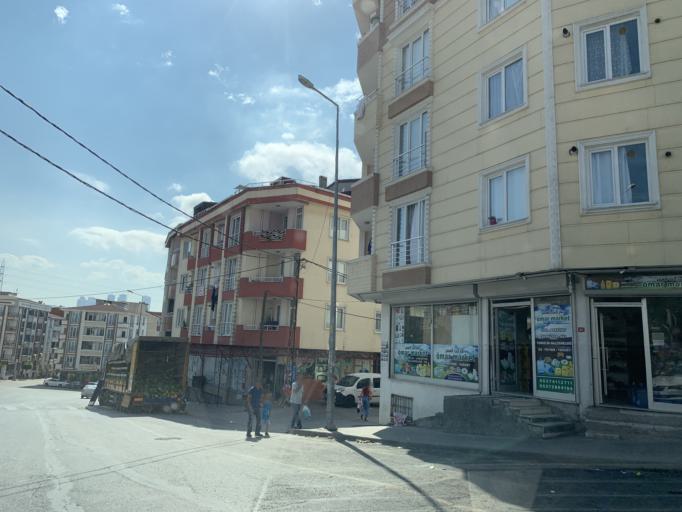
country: TR
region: Istanbul
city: Esenyurt
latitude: 41.0337
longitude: 28.6725
